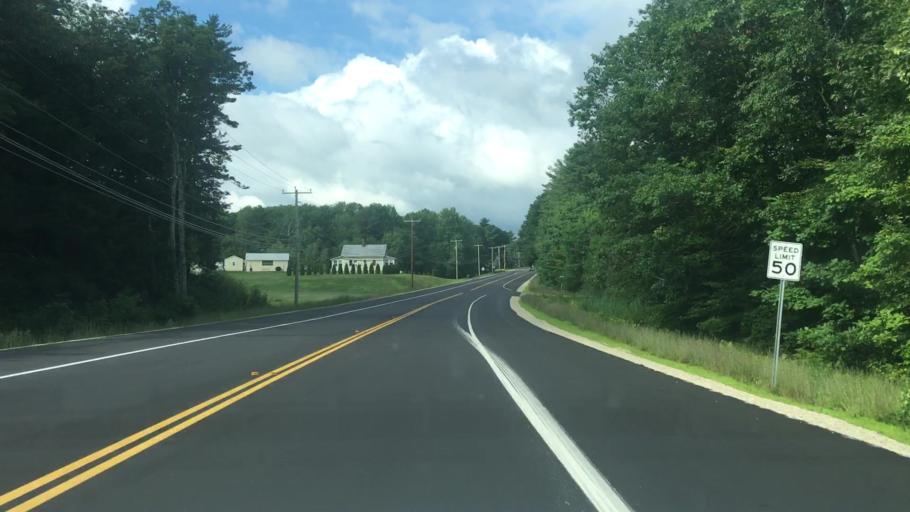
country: US
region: New Hampshire
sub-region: Belknap County
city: Gilford
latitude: 43.5450
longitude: -71.4108
